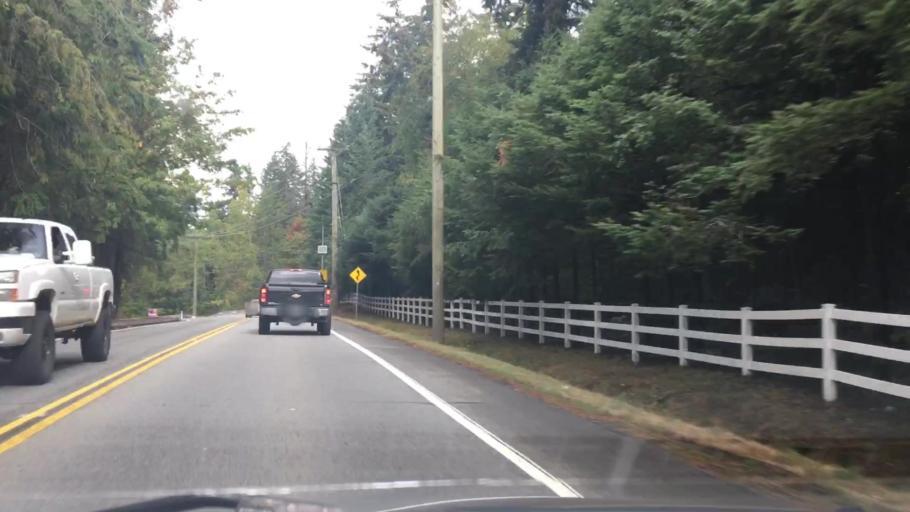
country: CA
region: British Columbia
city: Langley
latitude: 49.1049
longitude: -122.5650
